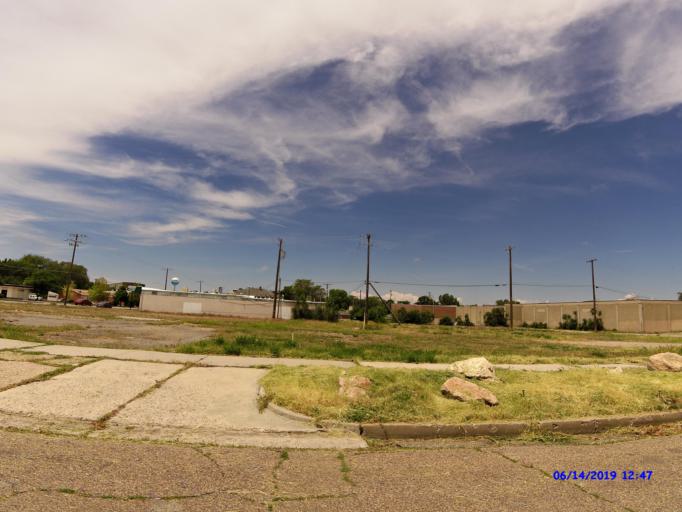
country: US
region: Utah
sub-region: Weber County
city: Ogden
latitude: 41.2211
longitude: -111.9566
